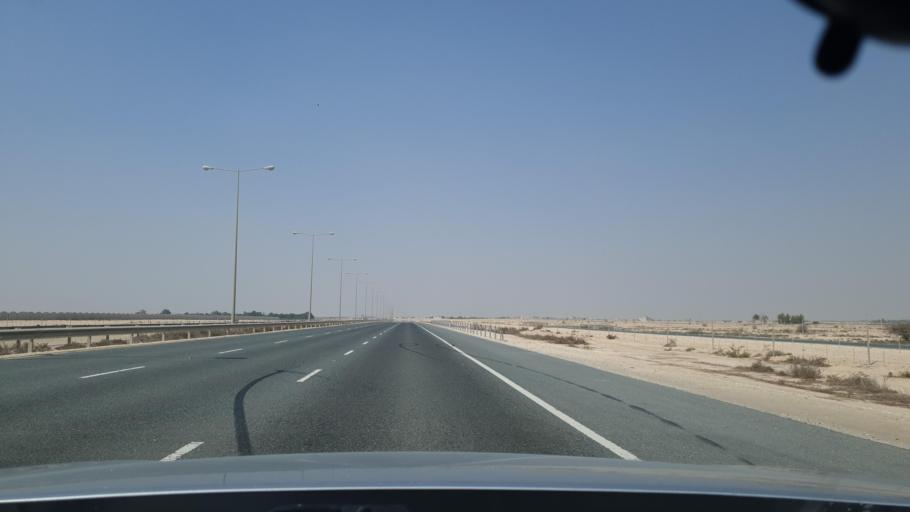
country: QA
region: Al Khawr
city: Al Khawr
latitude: 25.7694
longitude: 51.4158
